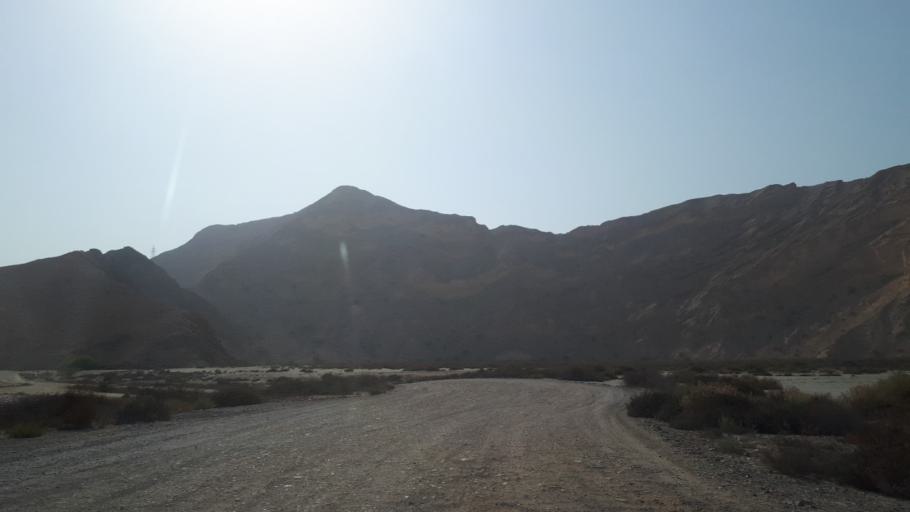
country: OM
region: Muhafazat Masqat
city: Muscat
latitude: 23.5396
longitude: 58.6600
